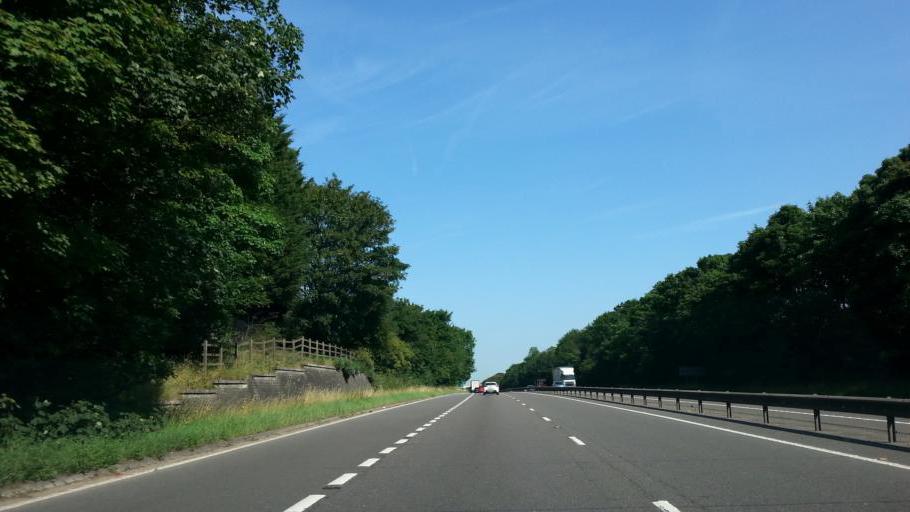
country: GB
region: England
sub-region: Nottinghamshire
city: Newark on Trent
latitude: 53.0802
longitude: -0.7727
